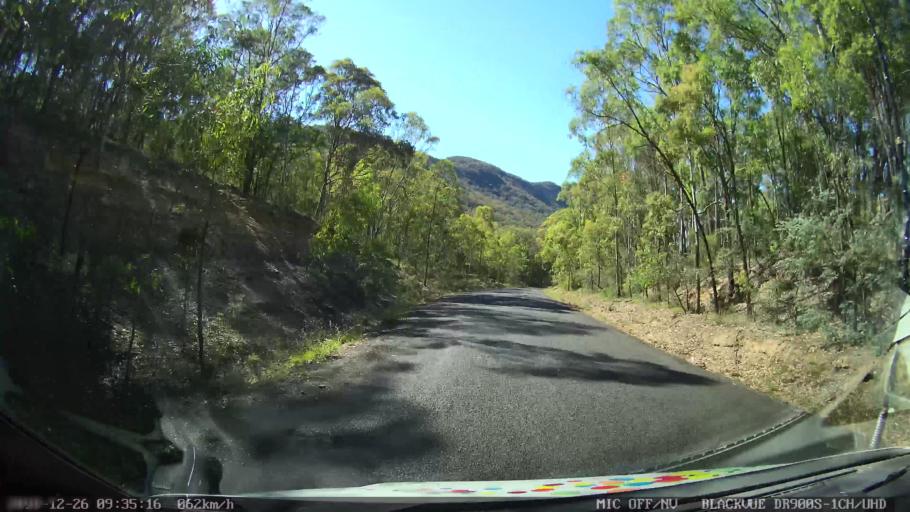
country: AU
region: New South Wales
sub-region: Mid-Western Regional
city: Kandos
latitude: -32.9128
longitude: 150.0402
